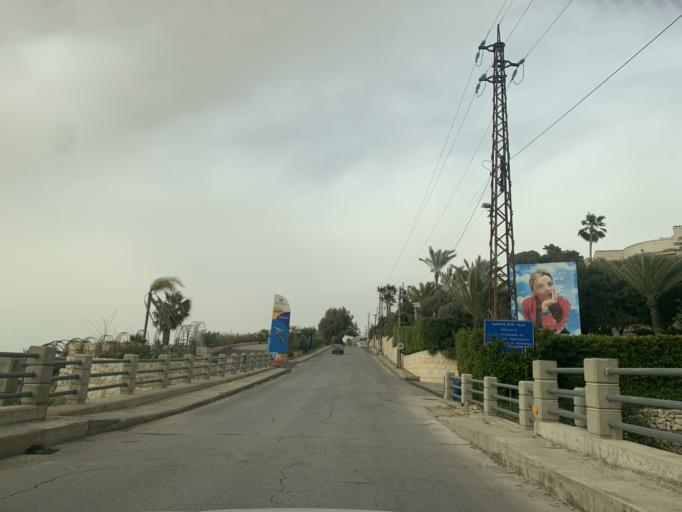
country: LB
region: Mont-Liban
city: Jbail
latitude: 34.1024
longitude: 35.6516
